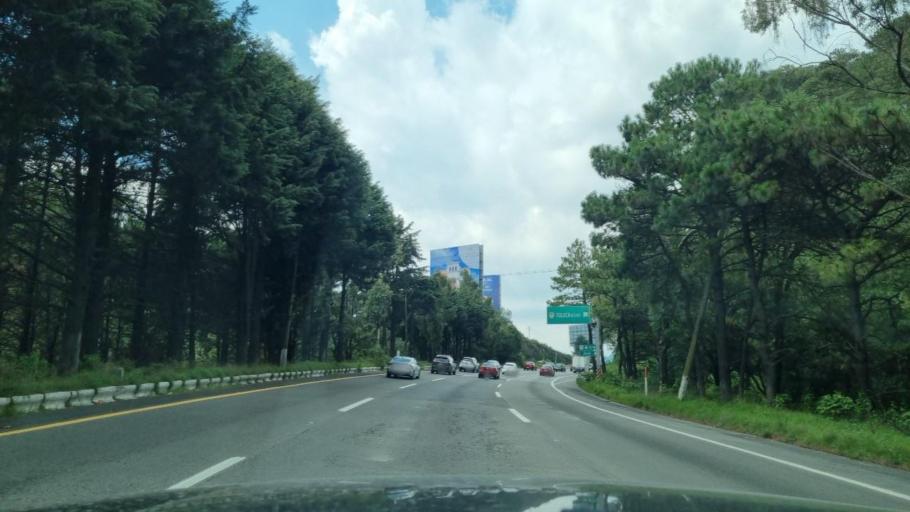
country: MX
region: Morelos
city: San Jeronimo Acazulco
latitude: 19.2973
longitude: -99.3963
